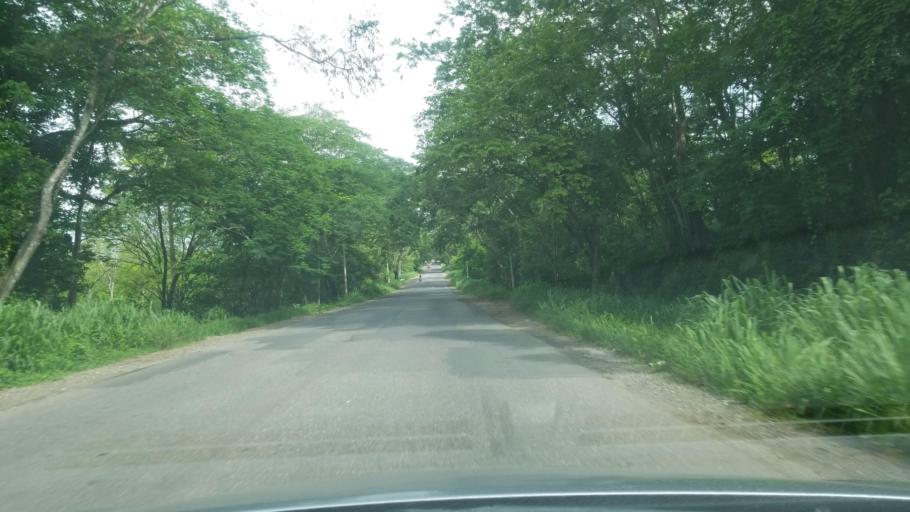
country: HN
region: Santa Barbara
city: Camalote
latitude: 15.3332
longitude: -88.3467
